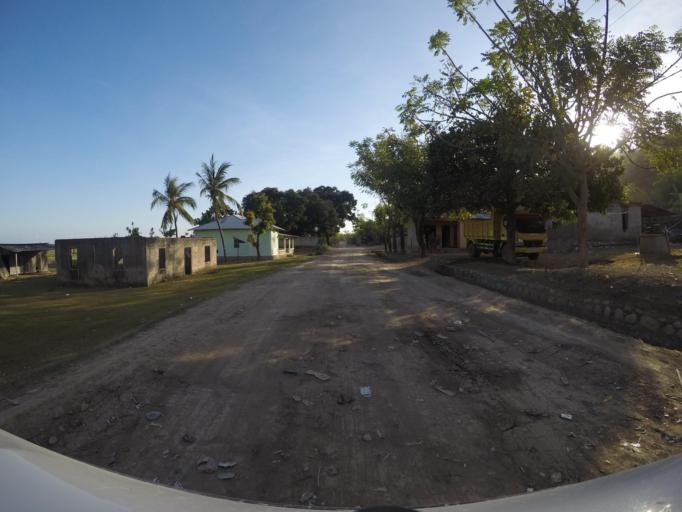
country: TL
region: Viqueque
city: Viqueque
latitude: -8.8008
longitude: 126.5521
